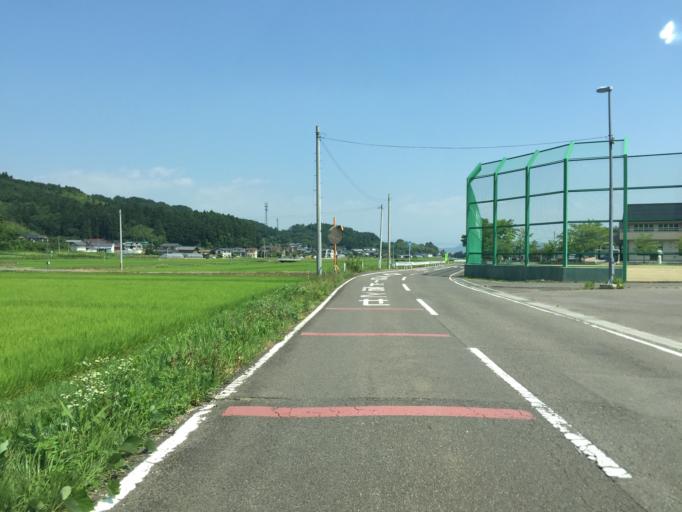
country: JP
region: Fukushima
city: Fukushima-shi
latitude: 37.6998
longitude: 140.4462
